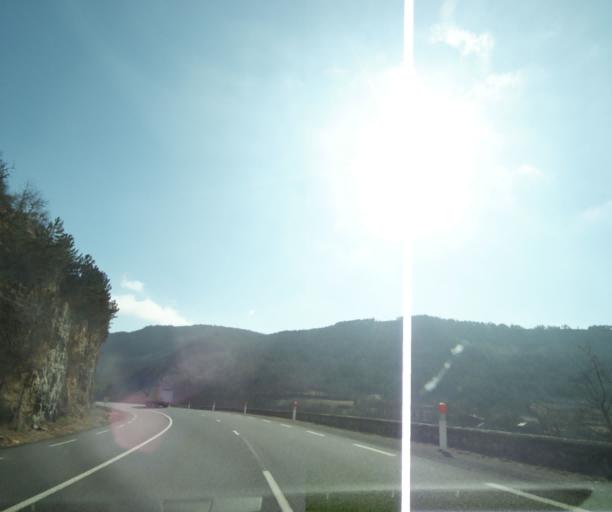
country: FR
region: Languedoc-Roussillon
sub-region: Departement de la Lozere
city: Mende
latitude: 44.4815
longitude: 3.4264
